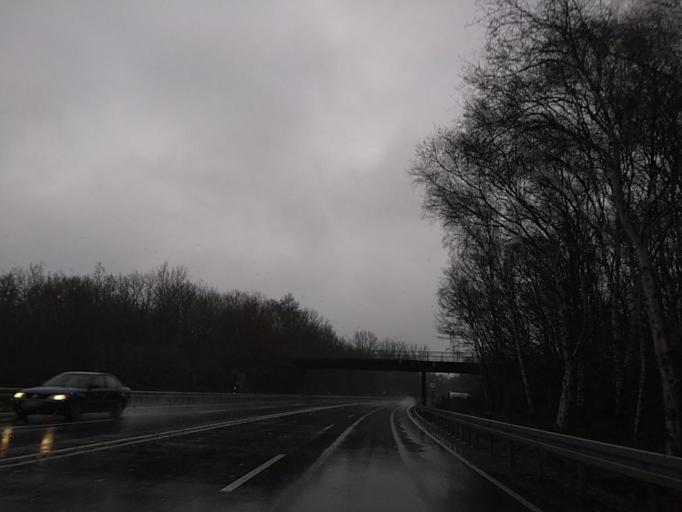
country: DE
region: Lower Saxony
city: Leer
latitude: 53.2384
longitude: 7.4416
